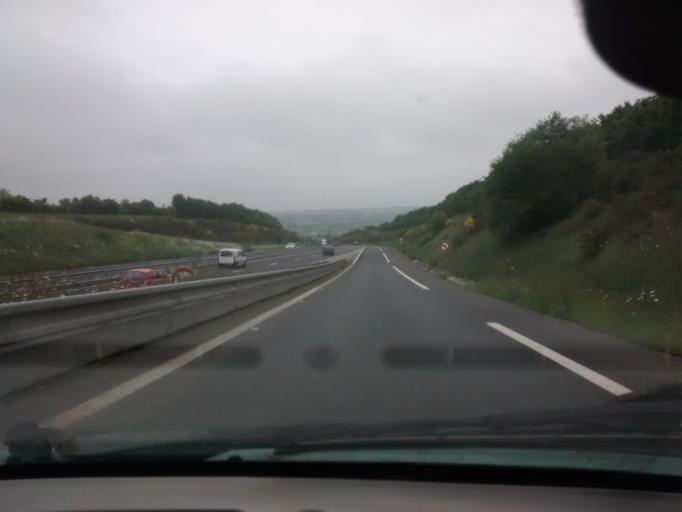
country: FR
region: Lower Normandy
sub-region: Departement de la Manche
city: Torigni-sur-Vire
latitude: 49.0507
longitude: -1.0036
